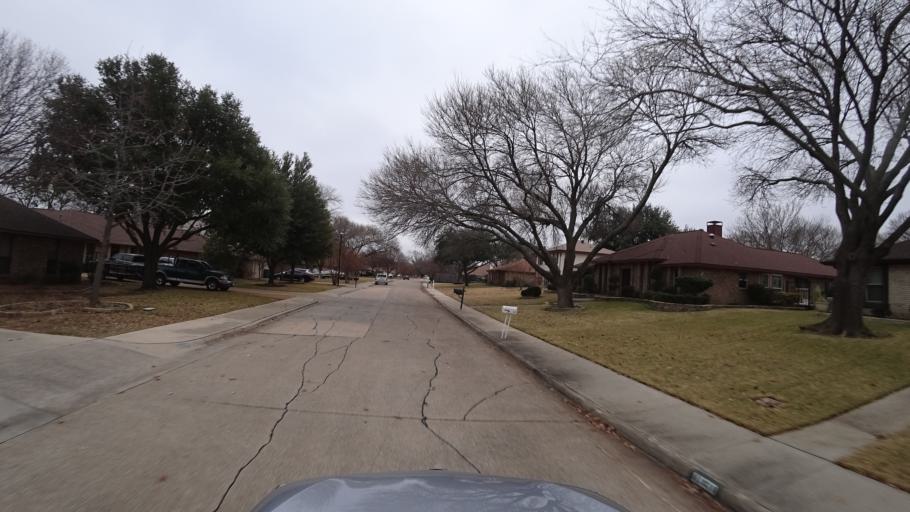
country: US
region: Texas
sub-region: Denton County
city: Highland Village
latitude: 33.0535
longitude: -97.0410
